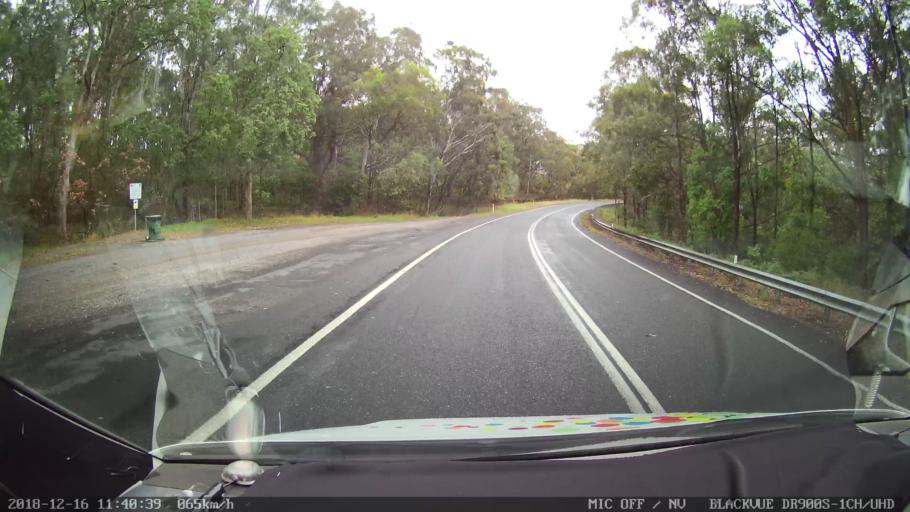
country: AU
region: New South Wales
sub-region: Tenterfield Municipality
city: Carrolls Creek
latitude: -28.9600
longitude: 152.2004
